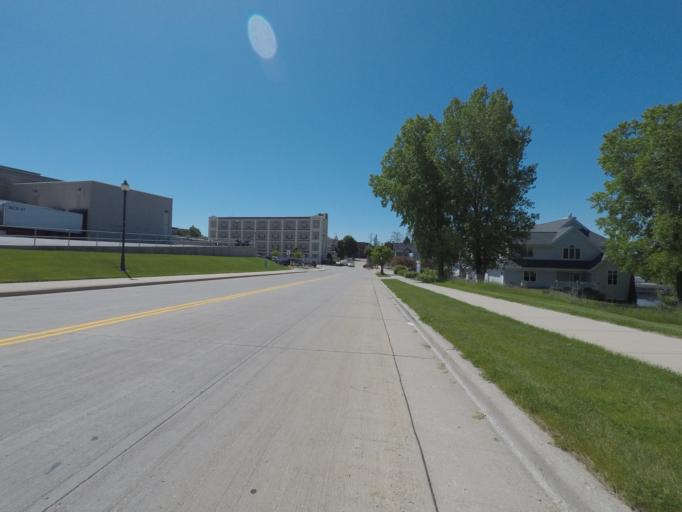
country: US
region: Wisconsin
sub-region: Sheboygan County
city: Sheboygan
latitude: 43.7507
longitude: -87.7159
